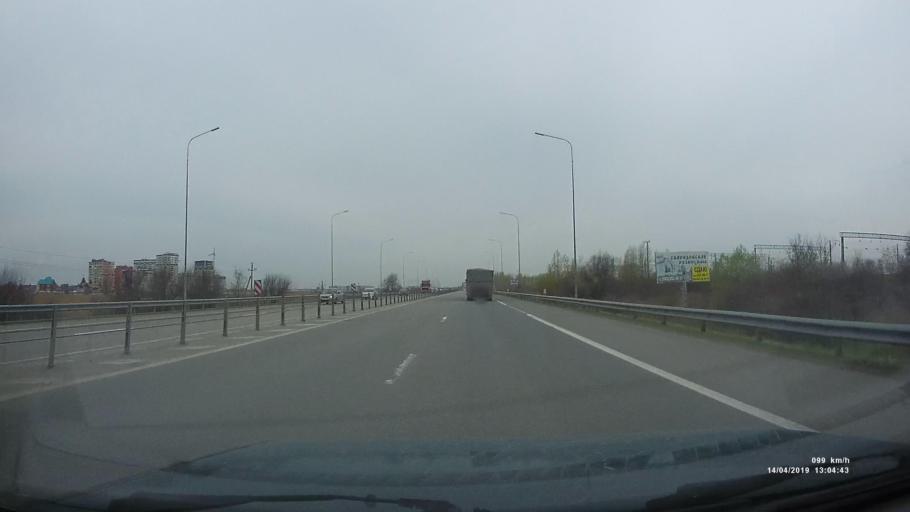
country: RU
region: Rostov
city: Bataysk
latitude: 47.1560
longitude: 39.7248
